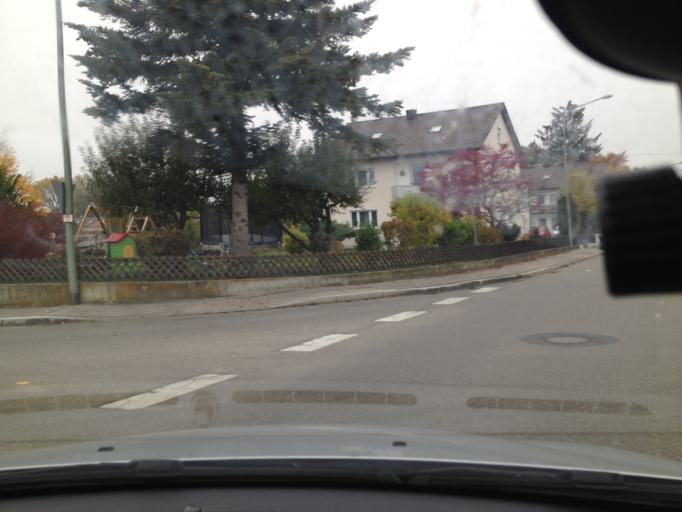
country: DE
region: Bavaria
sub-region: Swabia
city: Schwabmunchen
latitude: 48.1720
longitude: 10.7560
